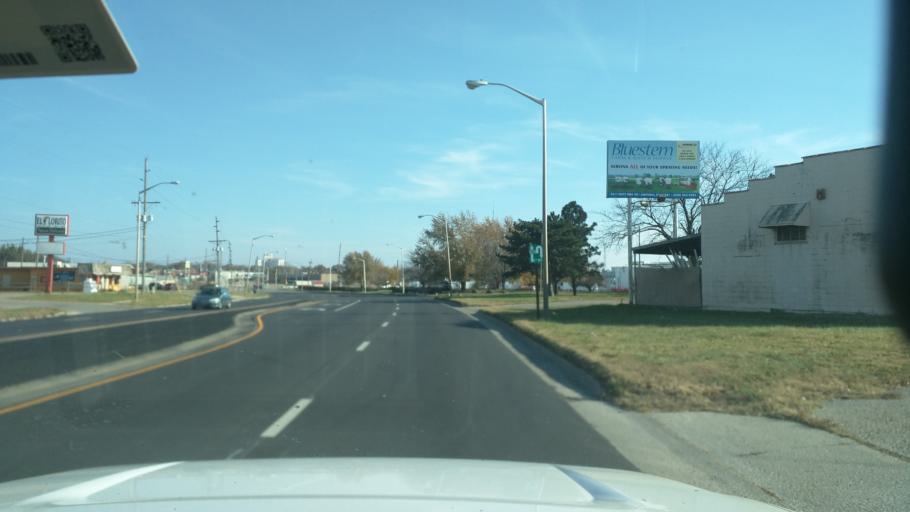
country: US
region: Kansas
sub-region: Lyon County
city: Emporia
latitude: 38.4060
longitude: -96.2119
